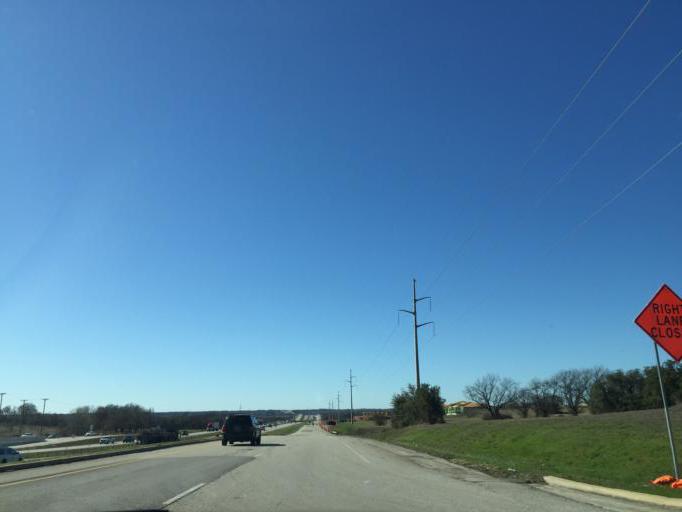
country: US
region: Texas
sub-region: Parker County
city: Hudson Oaks
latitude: 32.7530
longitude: -97.7123
